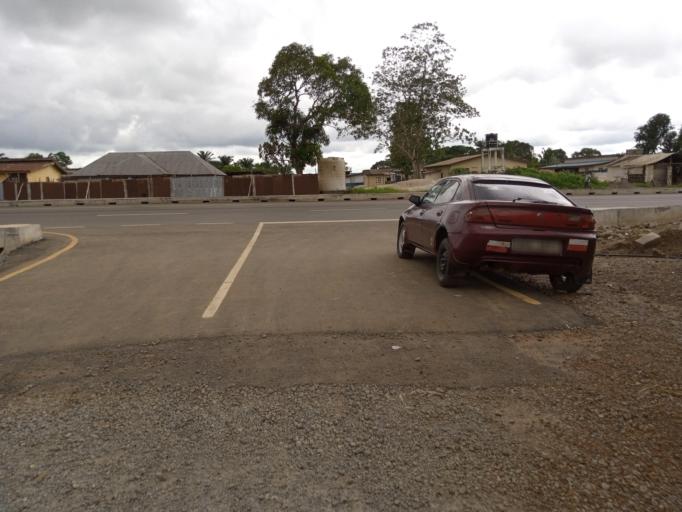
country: SL
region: Southern Province
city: Moyamba
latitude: 8.1645
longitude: -12.4254
